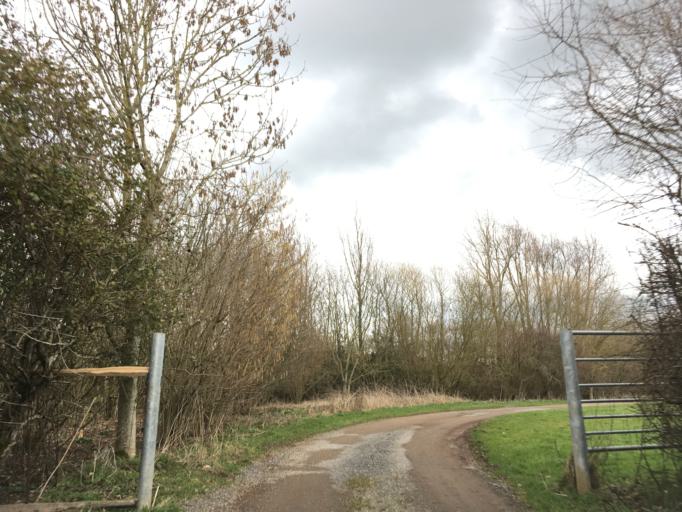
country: GB
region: England
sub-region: South Gloucestershire
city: Tytherington
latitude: 51.5769
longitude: -2.5021
